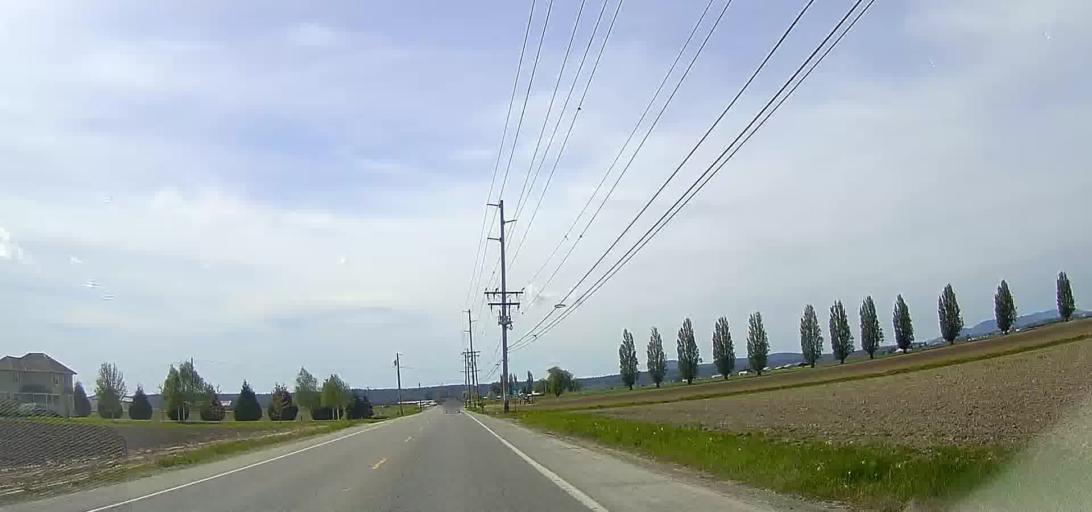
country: US
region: Washington
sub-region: Skagit County
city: Mount Vernon
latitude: 48.4206
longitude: -122.4389
